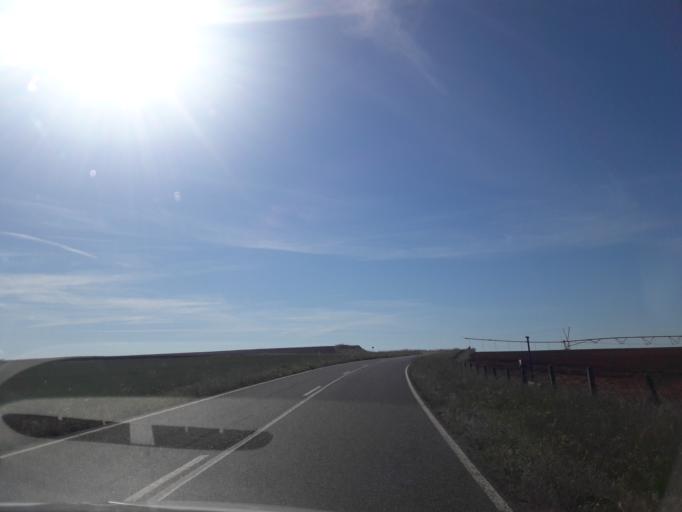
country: ES
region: Castille and Leon
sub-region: Provincia de Salamanca
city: Aldeanueva de Figueroa
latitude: 41.1473
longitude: -5.5183
